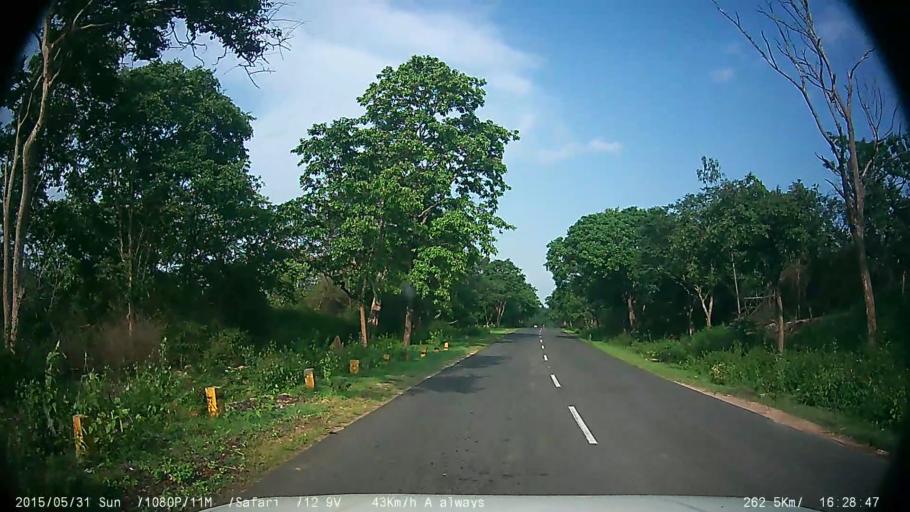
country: IN
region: Karnataka
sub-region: Chamrajnagar
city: Gundlupet
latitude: 11.7693
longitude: 76.5439
